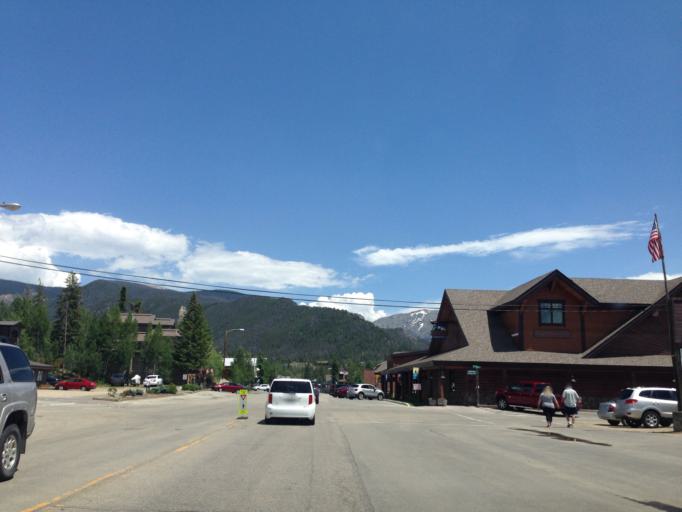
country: US
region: Colorado
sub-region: Grand County
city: Granby
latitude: 40.2523
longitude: -105.8235
